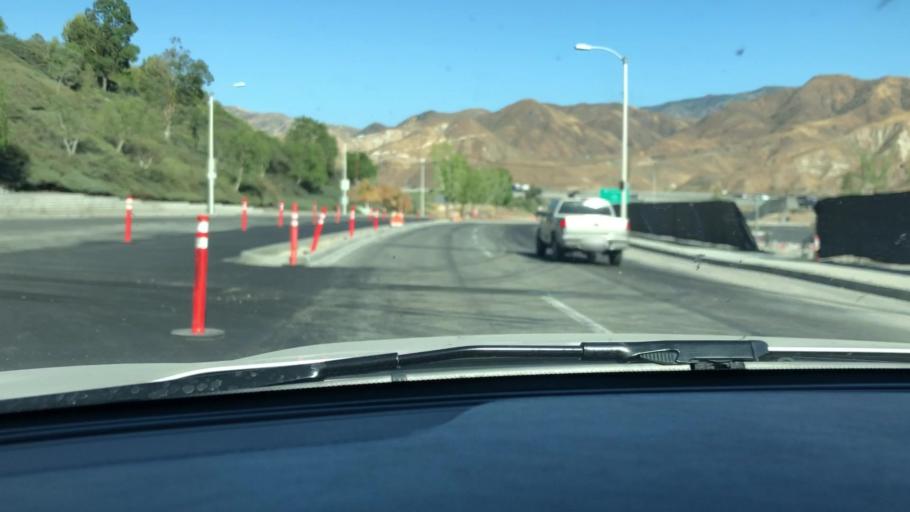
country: US
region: California
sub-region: Los Angeles County
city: Agua Dulce
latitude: 34.4352
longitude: -118.3881
